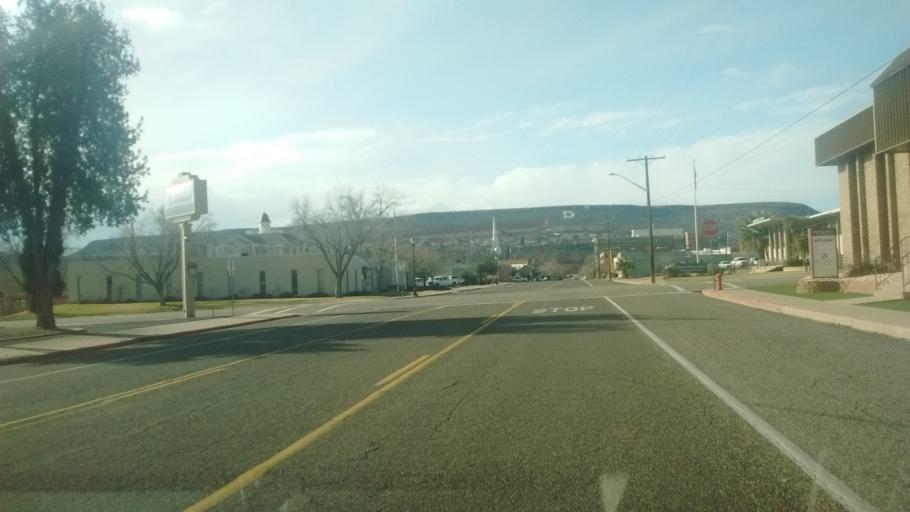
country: US
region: Utah
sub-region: Washington County
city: Saint George
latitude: 37.1082
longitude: -113.5785
